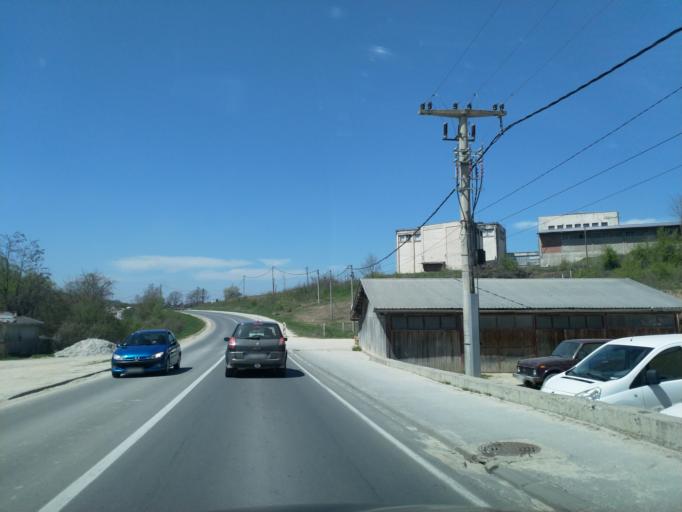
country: RS
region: Central Serbia
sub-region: Sumadijski Okrug
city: Arangelovac
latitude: 44.3257
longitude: 20.5274
